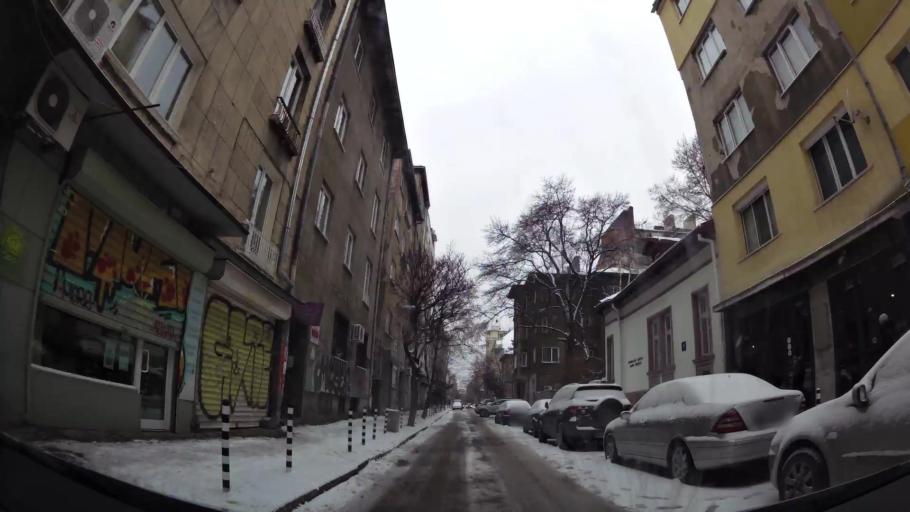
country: BG
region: Sofia-Capital
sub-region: Stolichna Obshtina
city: Sofia
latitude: 42.6938
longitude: 23.3167
